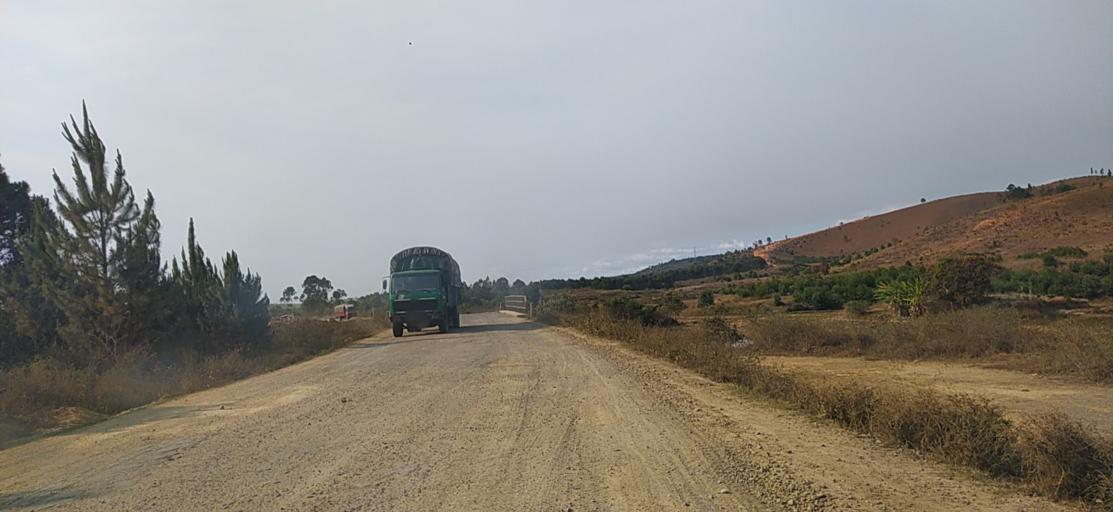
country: MG
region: Alaotra Mangoro
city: Moramanga
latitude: -18.6669
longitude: 48.2747
